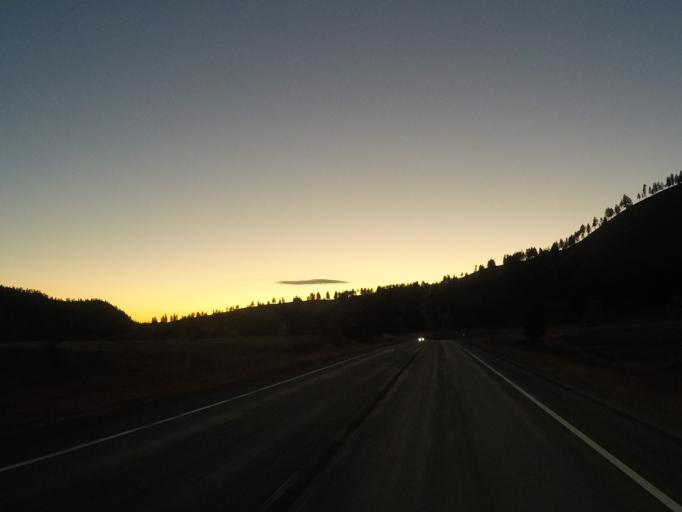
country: US
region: Montana
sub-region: Missoula County
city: Seeley Lake
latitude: 47.0302
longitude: -113.2746
